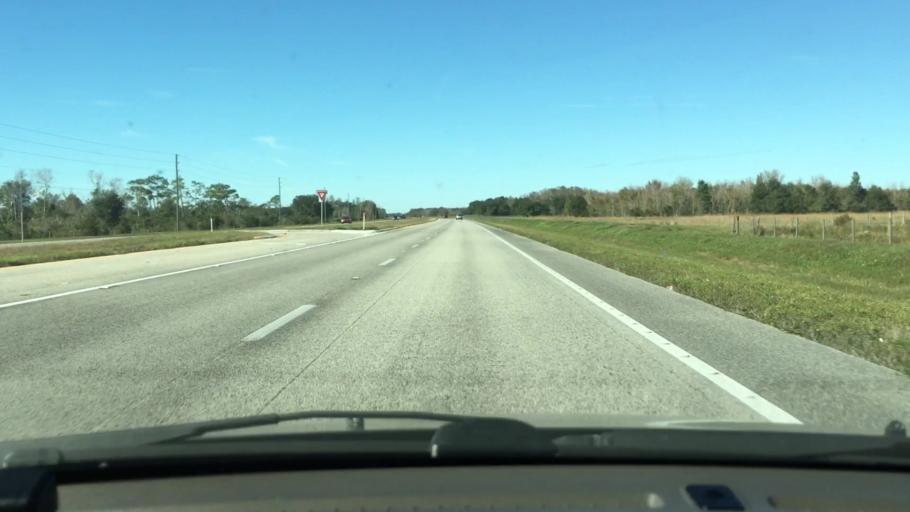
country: US
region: Florida
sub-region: Brevard County
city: June Park
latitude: 28.1271
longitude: -80.9789
